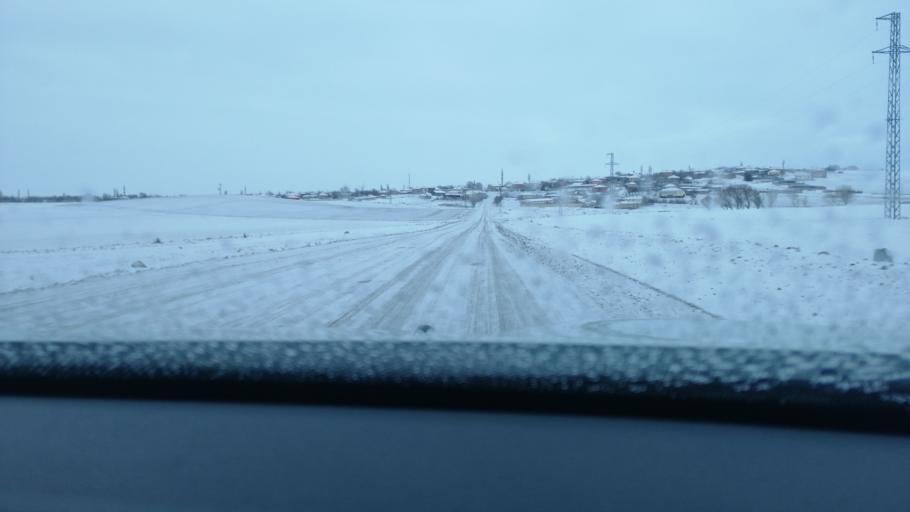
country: TR
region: Aksaray
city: Agacoren
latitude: 38.9414
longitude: 33.9474
